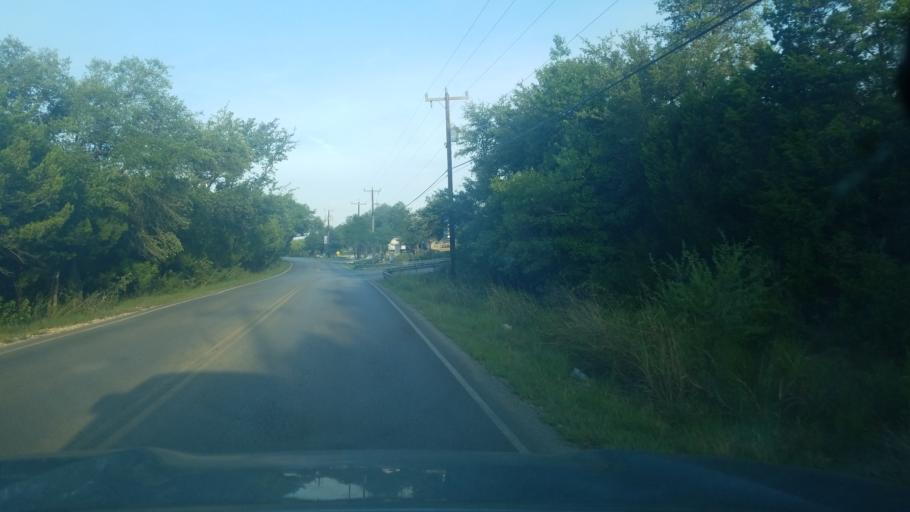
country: US
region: Texas
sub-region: Comal County
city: Bulverde
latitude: 29.7424
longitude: -98.4392
